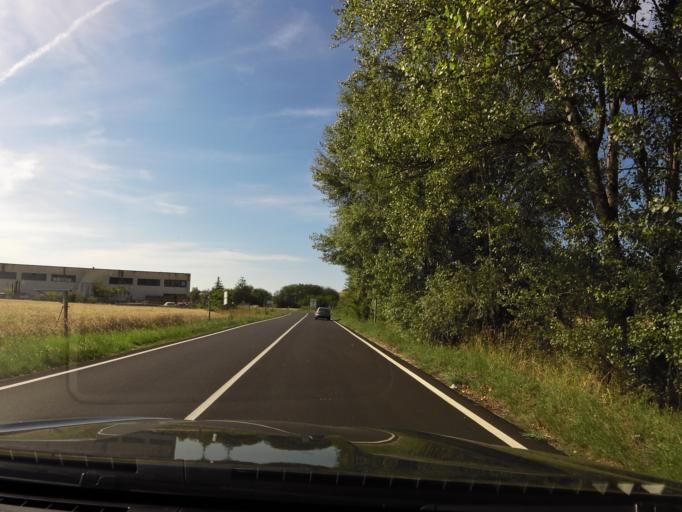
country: IT
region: The Marches
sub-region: Provincia di Ancona
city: Camerano
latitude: 43.5220
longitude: 13.5274
